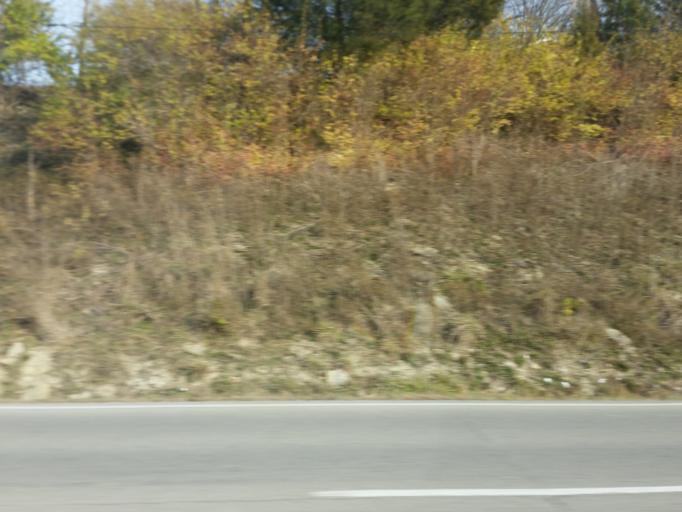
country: US
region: Kentucky
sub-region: Campbell County
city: Claryville
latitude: 38.8147
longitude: -84.3575
